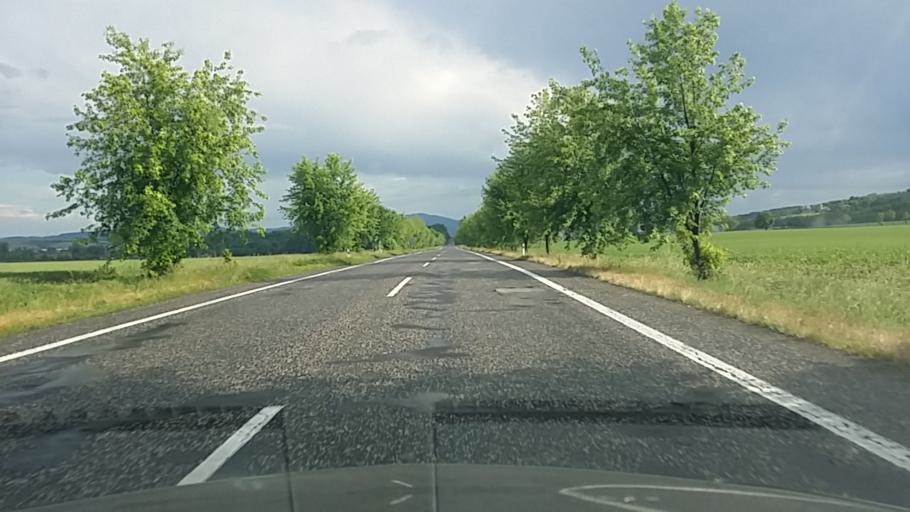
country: SK
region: Banskobystricky
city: Dudince
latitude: 48.1377
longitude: 18.8748
